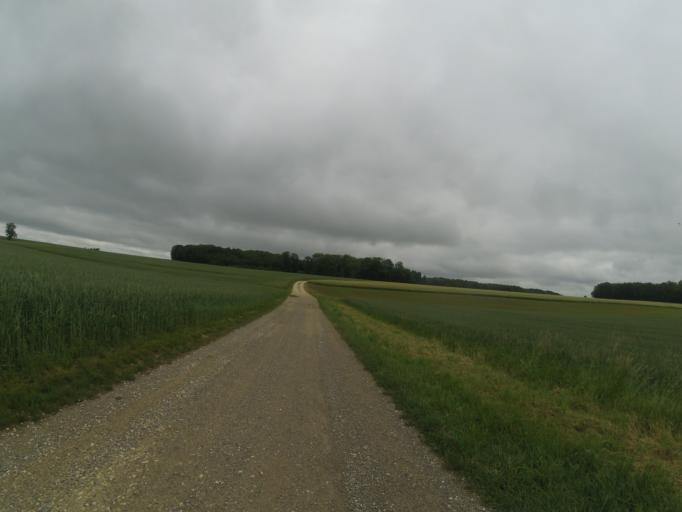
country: DE
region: Baden-Wuerttemberg
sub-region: Tuebingen Region
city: Bernstadt
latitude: 48.4570
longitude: 10.0499
